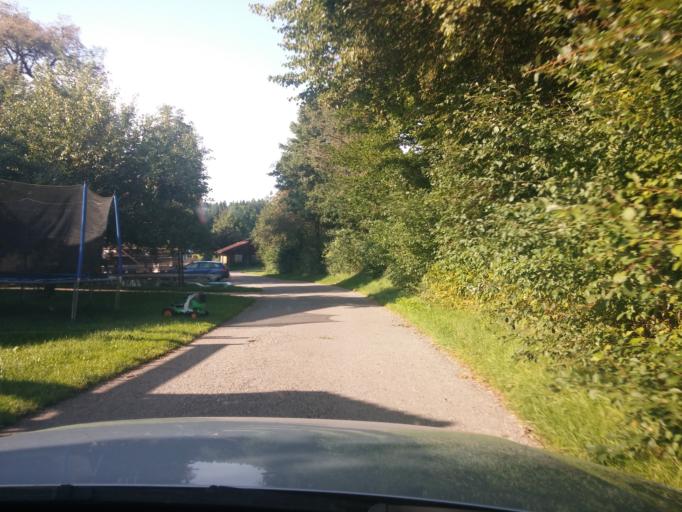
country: DE
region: Bavaria
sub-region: Swabia
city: Lautrach
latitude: 47.8738
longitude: 10.1099
